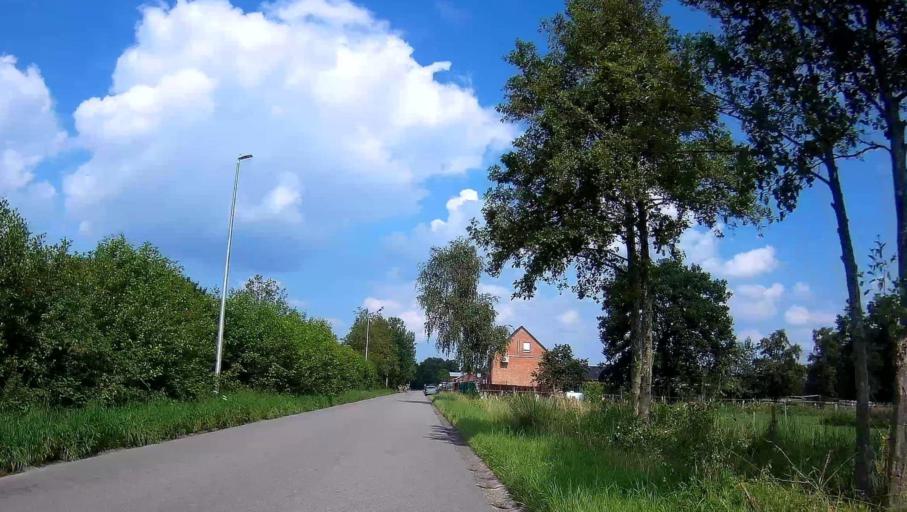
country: BE
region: Flanders
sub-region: Provincie Limburg
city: Leopoldsburg
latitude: 51.1751
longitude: 5.2728
